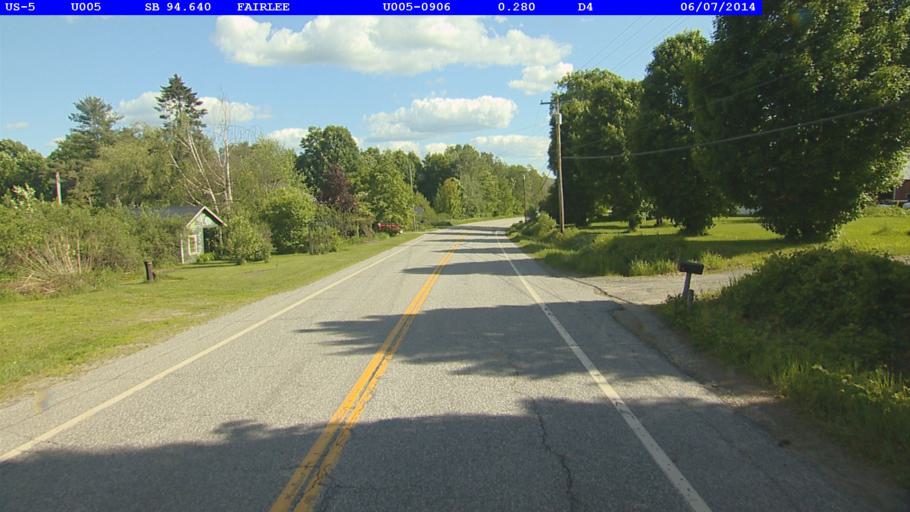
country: US
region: New Hampshire
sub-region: Grafton County
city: Orford
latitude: 43.8782
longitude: -72.1763
